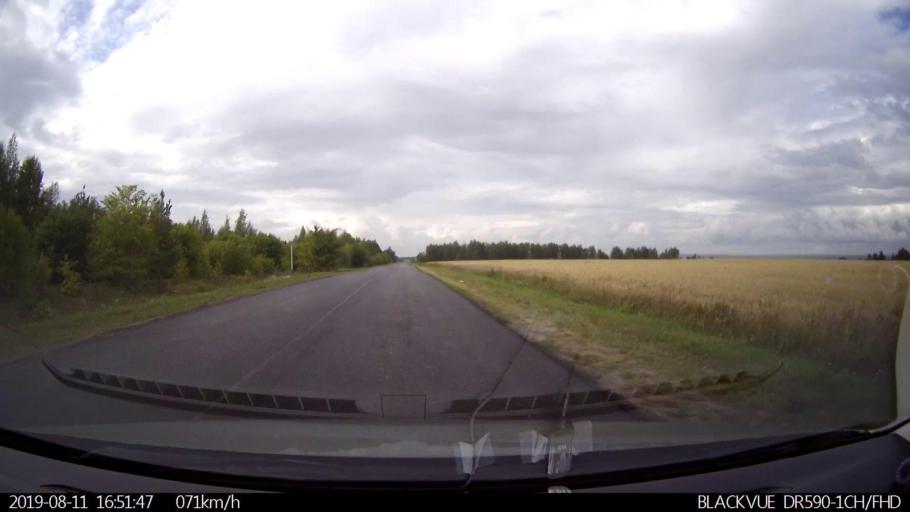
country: RU
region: Ulyanovsk
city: Mayna
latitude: 54.2408
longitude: 47.6760
